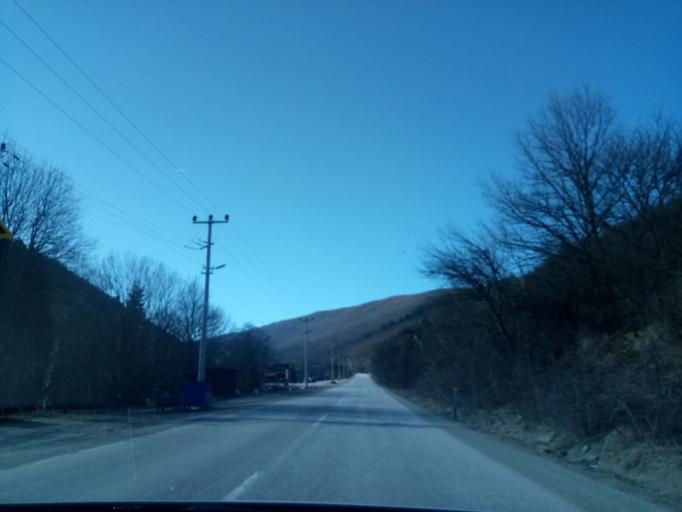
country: TR
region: Duzce
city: Kaynasli
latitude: 40.6613
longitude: 31.4074
